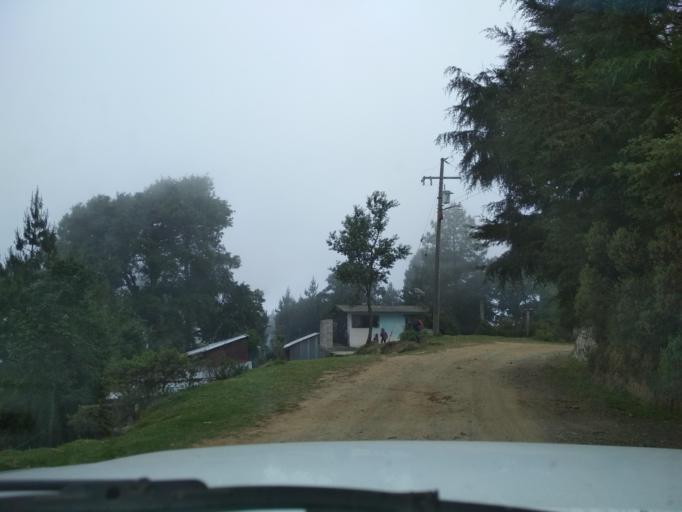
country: MX
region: Veracruz
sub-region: Mariano Escobedo
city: San Isidro el Berro
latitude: 18.9303
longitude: -97.2189
